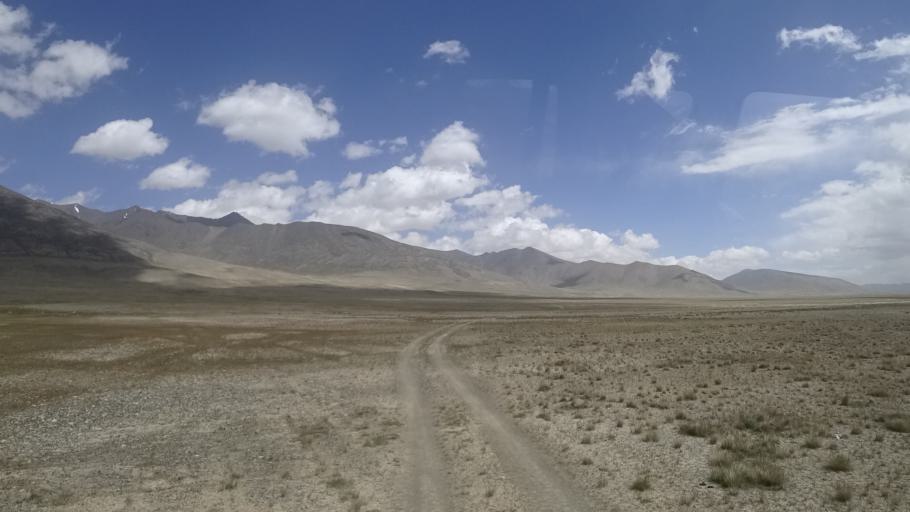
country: TJ
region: Gorno-Badakhshan
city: Murghob
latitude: 37.4769
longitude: 73.9757
